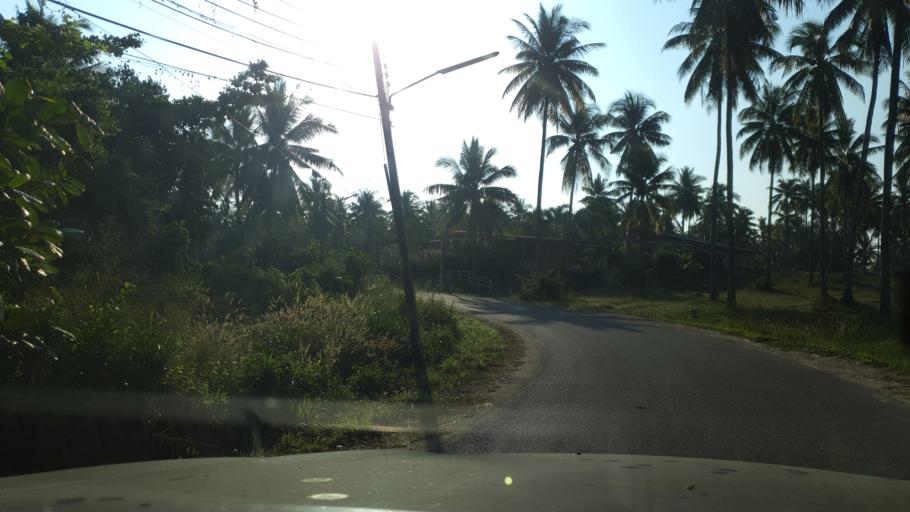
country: TH
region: Prachuap Khiri Khan
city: Bang Saphan
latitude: 11.2129
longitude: 99.5762
